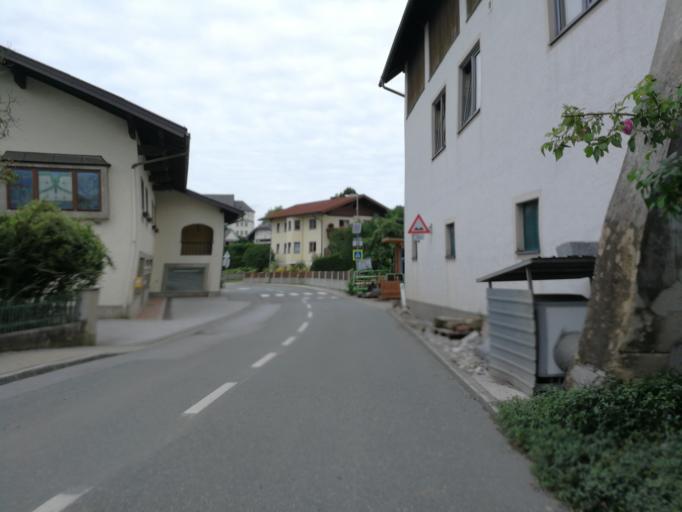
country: DE
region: Bavaria
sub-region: Upper Bavaria
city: Ainring
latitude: 47.7896
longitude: 12.9654
